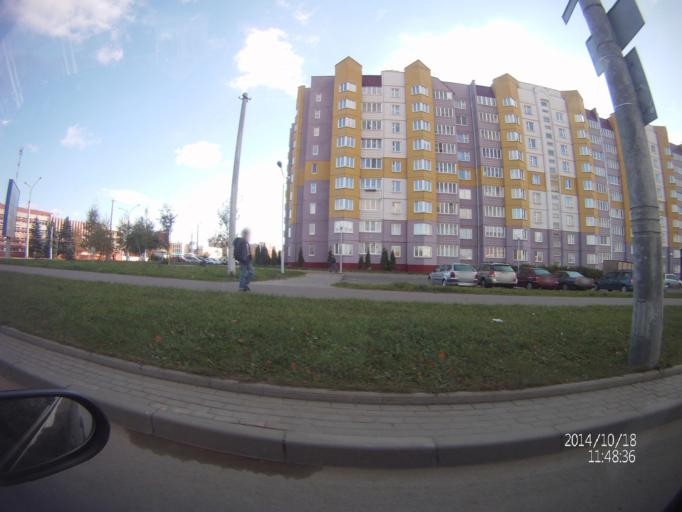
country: BY
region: Minsk
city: Novoye Medvezhino
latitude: 53.8805
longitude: 27.4852
